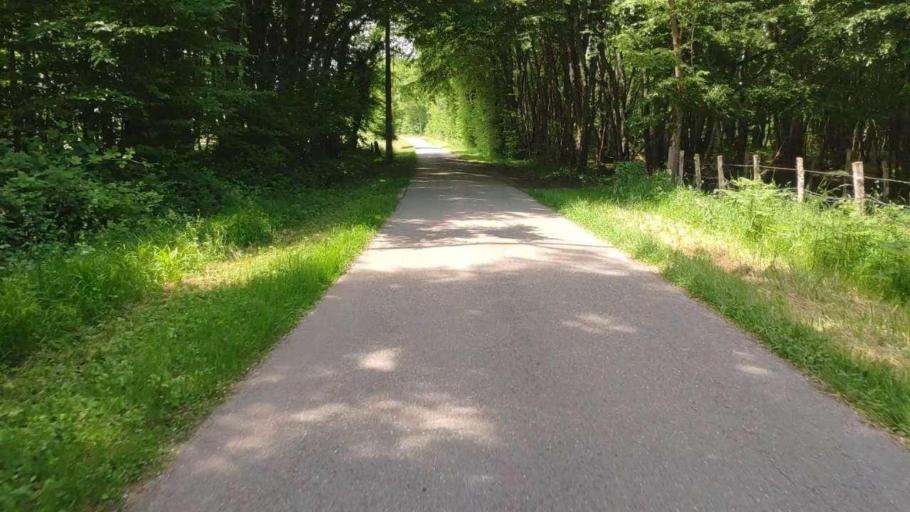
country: FR
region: Franche-Comte
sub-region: Departement du Jura
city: Bletterans
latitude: 46.7728
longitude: 5.4409
